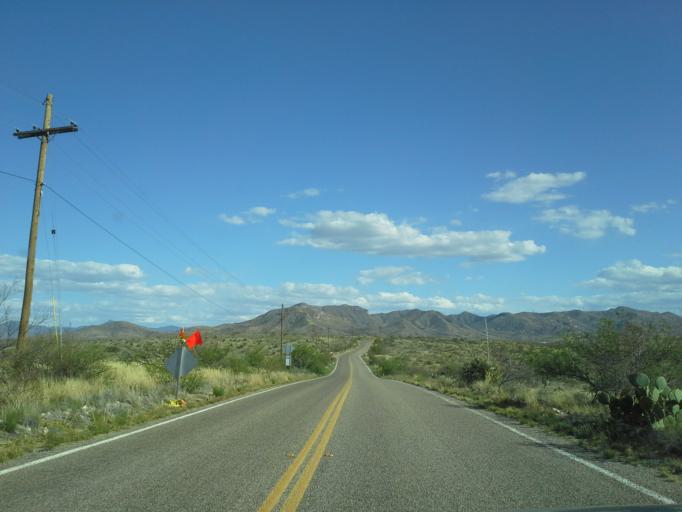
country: US
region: Arizona
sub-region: Pima County
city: Vail
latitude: 31.9686
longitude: -110.6608
